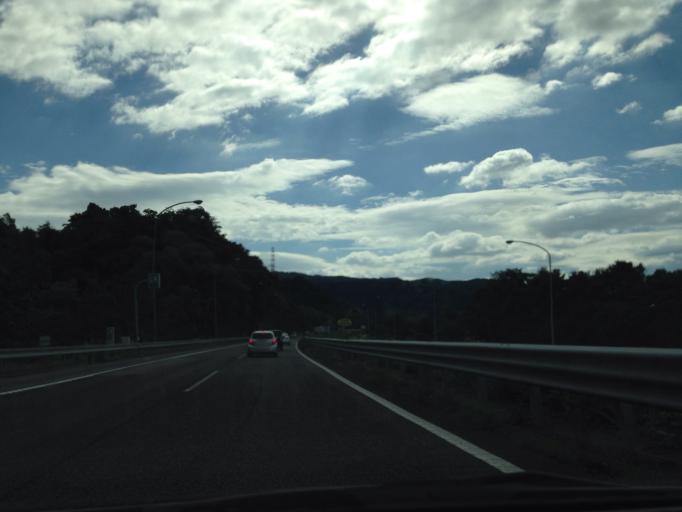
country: JP
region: Shizuoka
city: Gotemba
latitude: 35.3594
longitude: 139.0173
